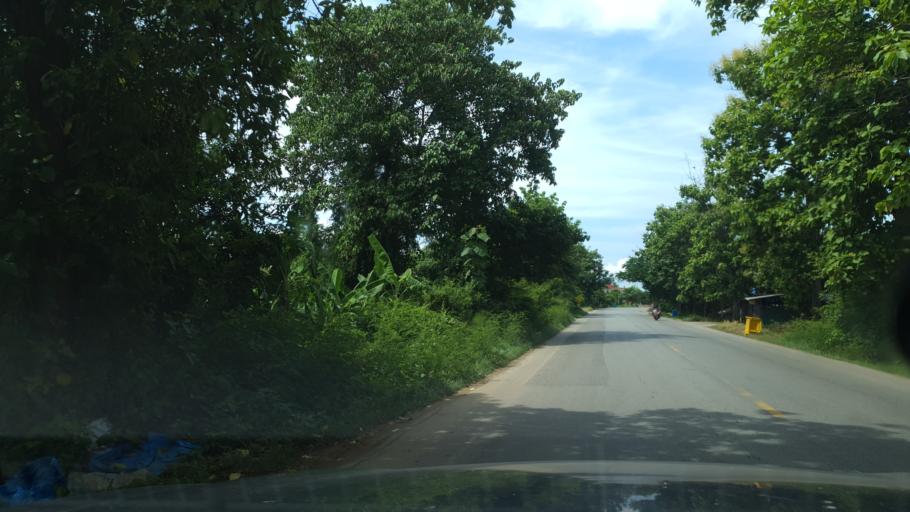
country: TH
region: Sukhothai
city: Sukhothai
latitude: 17.0635
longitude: 99.8297
